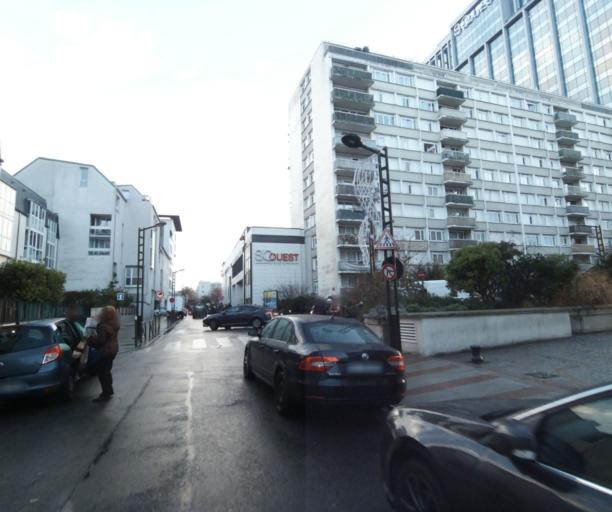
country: FR
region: Ile-de-France
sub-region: Departement des Hauts-de-Seine
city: Levallois-Perret
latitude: 48.8939
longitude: 2.2976
